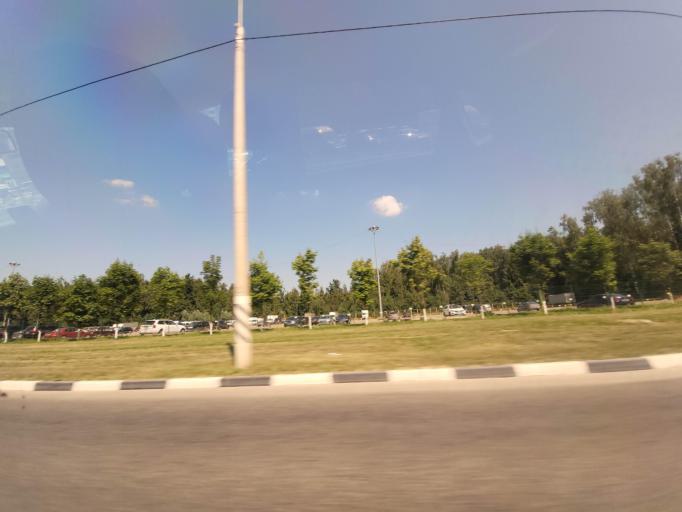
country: RU
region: Kaluga
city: Obninsk
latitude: 55.1246
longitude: 36.6218
